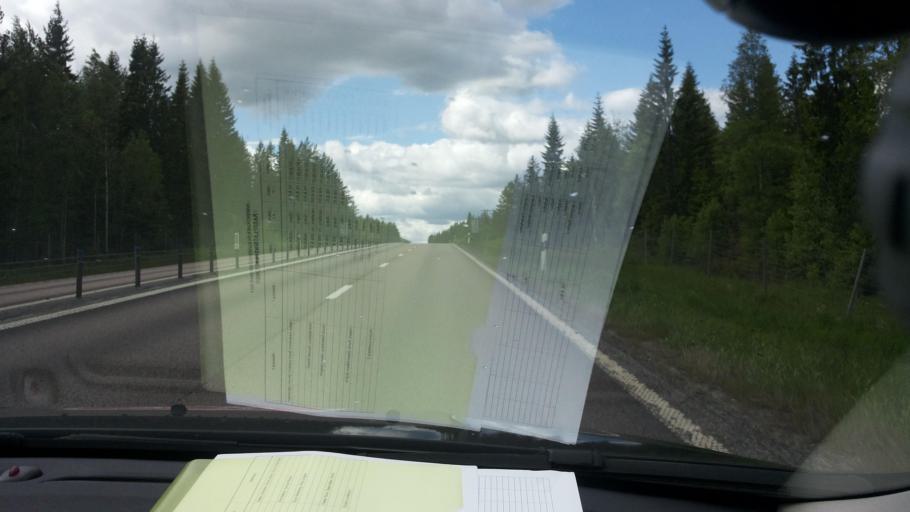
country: SE
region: Vaesternorrland
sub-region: Timra Kommun
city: Soraker
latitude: 62.5346
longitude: 17.5293
